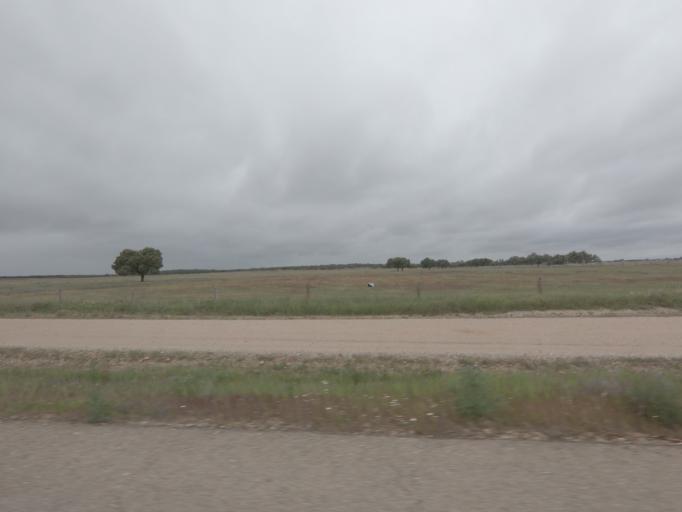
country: ES
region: Extremadura
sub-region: Provincia de Badajoz
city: Badajoz
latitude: 38.9767
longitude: -6.8879
